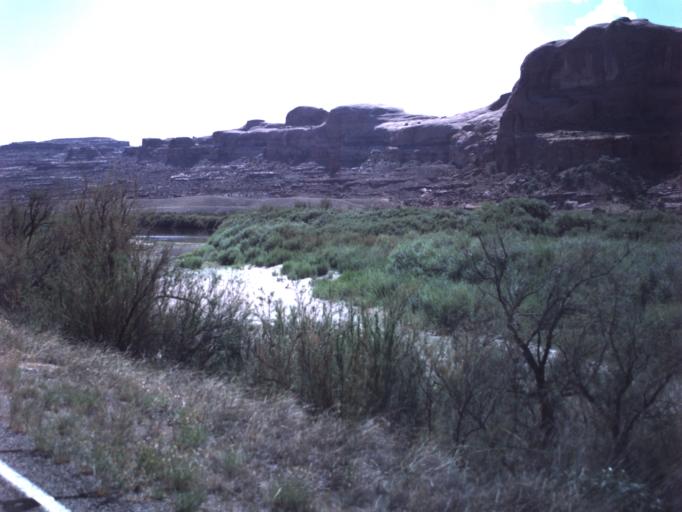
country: US
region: Utah
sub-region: Grand County
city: Moab
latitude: 38.5658
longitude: -109.6317
